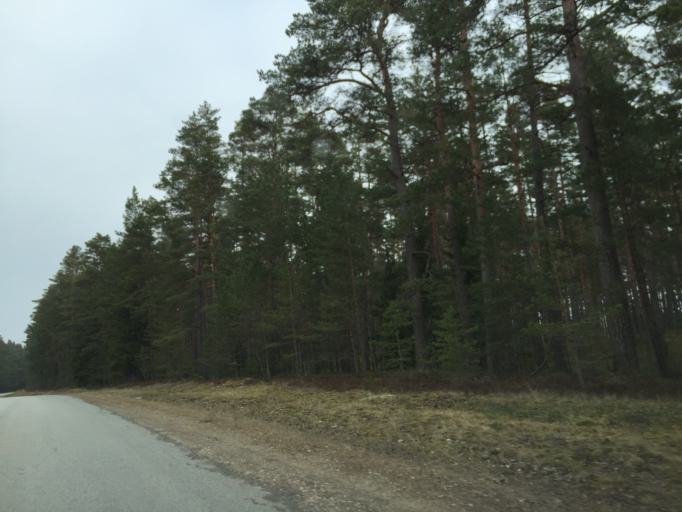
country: LV
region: Salacgrivas
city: Ainazi
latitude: 57.9800
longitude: 24.4158
